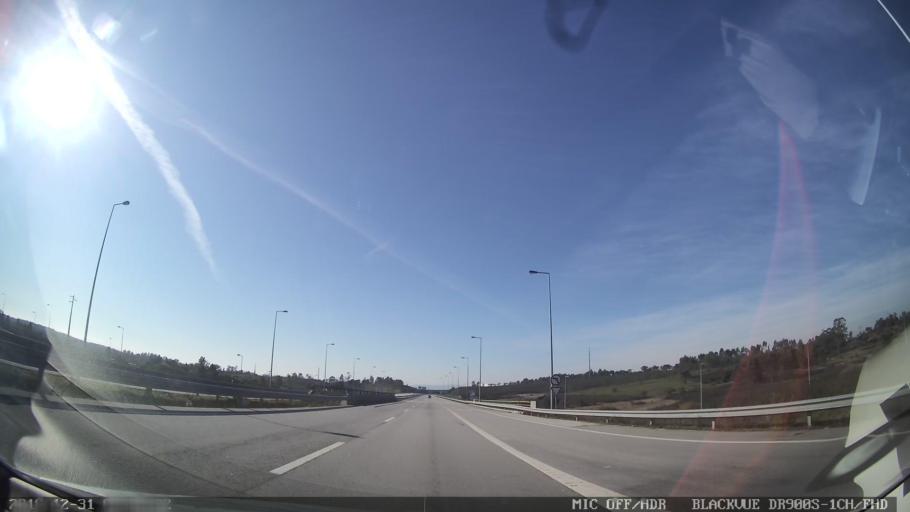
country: PT
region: Castelo Branco
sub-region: Castelo Branco
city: Castelo Branco
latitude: 39.7605
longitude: -7.6055
